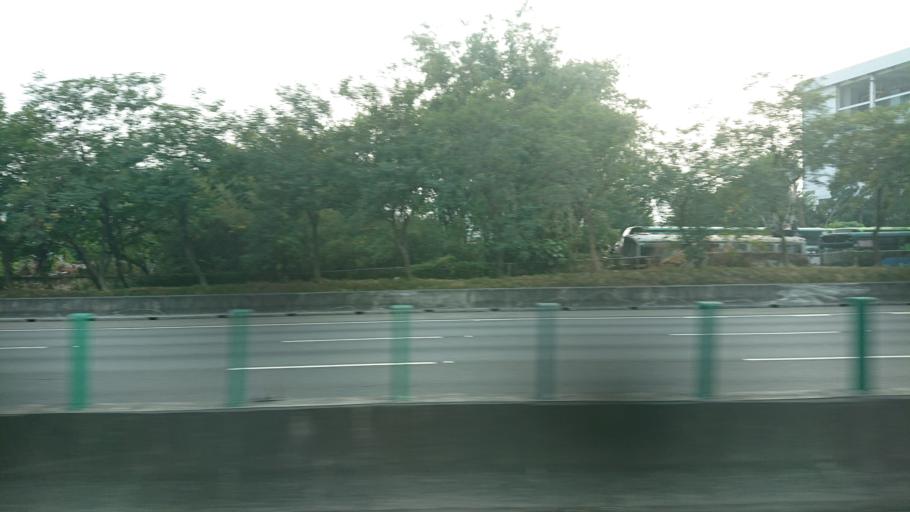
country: TW
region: Taiwan
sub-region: Changhua
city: Chang-hua
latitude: 24.1166
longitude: 120.5915
